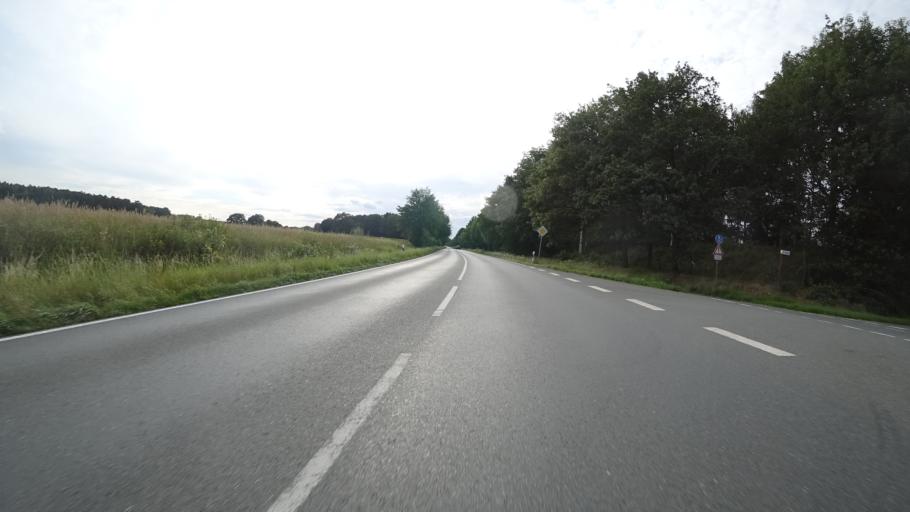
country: DE
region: North Rhine-Westphalia
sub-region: Regierungsbezirk Detmold
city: Harsewinkel
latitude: 51.9680
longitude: 8.1888
